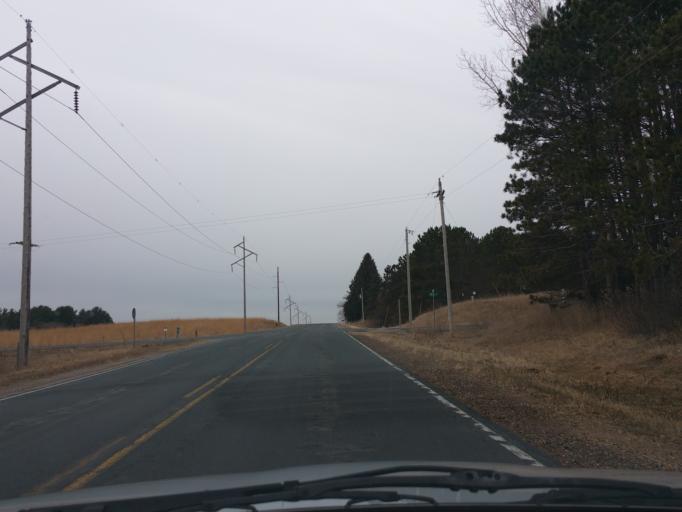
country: US
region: Wisconsin
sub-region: Saint Croix County
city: Roberts
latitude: 45.0358
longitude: -92.5774
